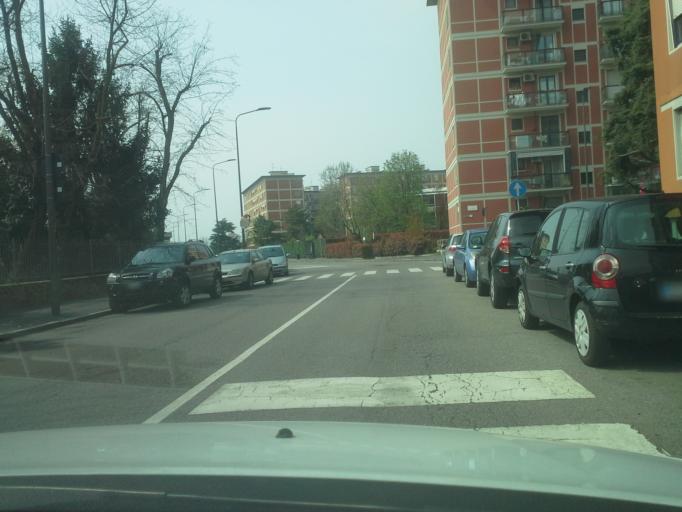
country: IT
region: Lombardy
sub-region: Citta metropolitana di Milano
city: Cesano Boscone
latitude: 45.4516
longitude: 9.0831
